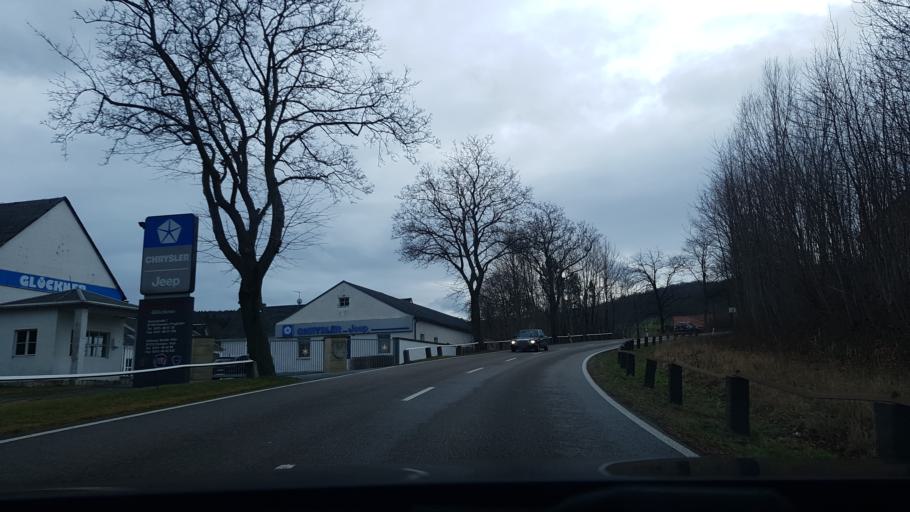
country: DE
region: Saxony
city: Dohma
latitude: 50.8725
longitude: 13.9567
